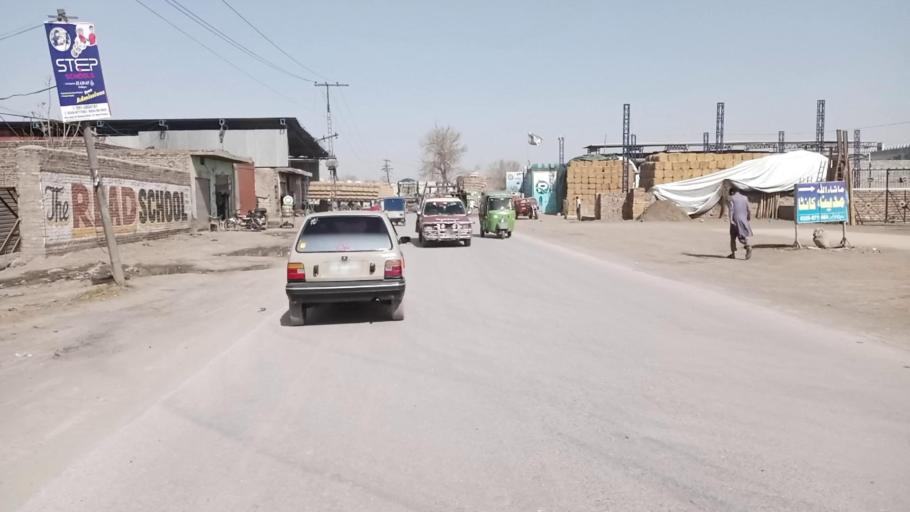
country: PK
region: Khyber Pakhtunkhwa
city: Peshawar
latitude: 34.0170
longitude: 71.6467
